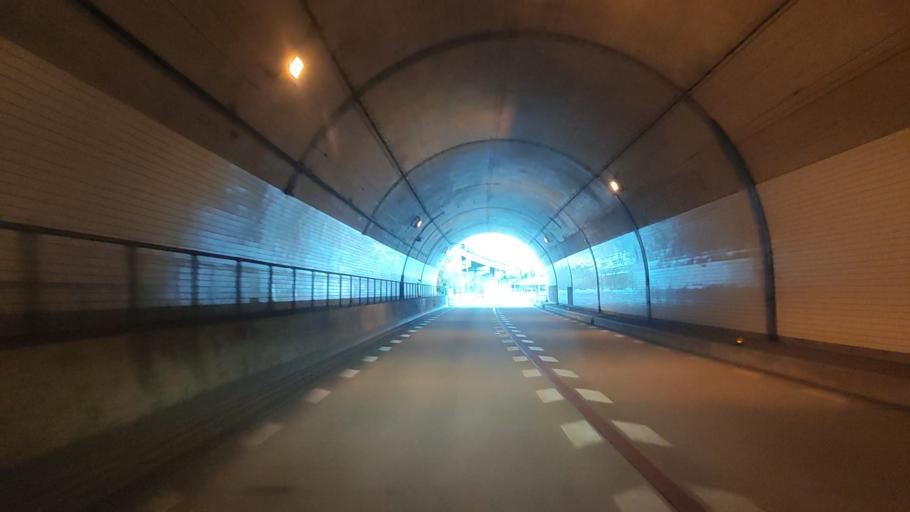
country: JP
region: Hyogo
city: Akashi
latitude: 34.6671
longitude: 135.0665
